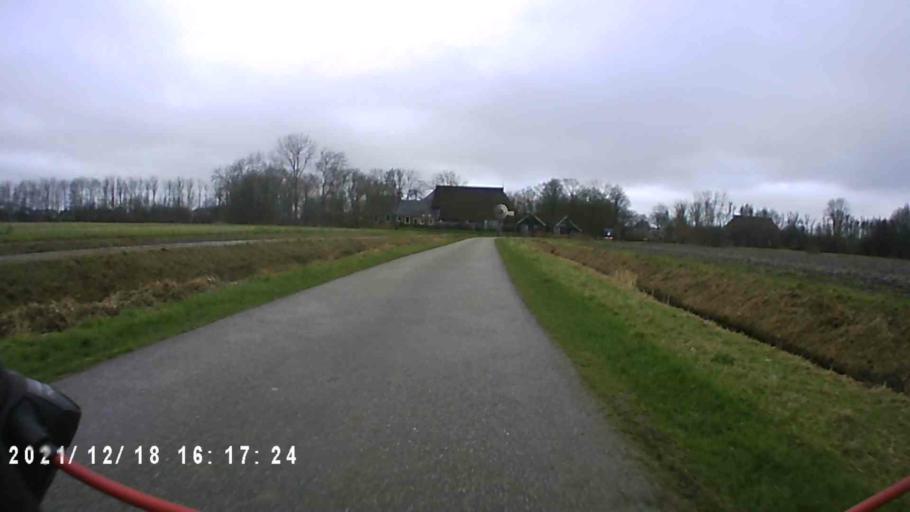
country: NL
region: Friesland
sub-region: Gemeente Dongeradeel
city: Anjum
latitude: 53.3750
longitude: 6.0583
